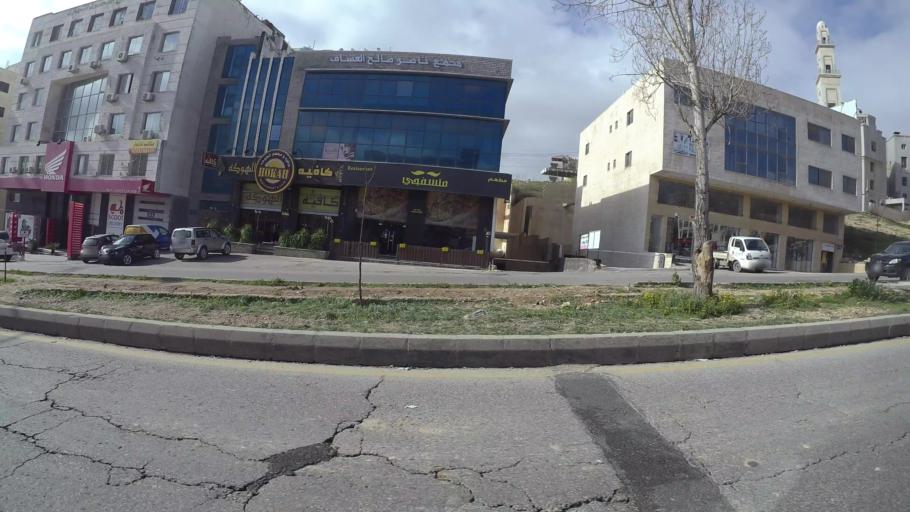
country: JO
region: Amman
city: Al Jubayhah
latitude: 31.9959
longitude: 35.8559
